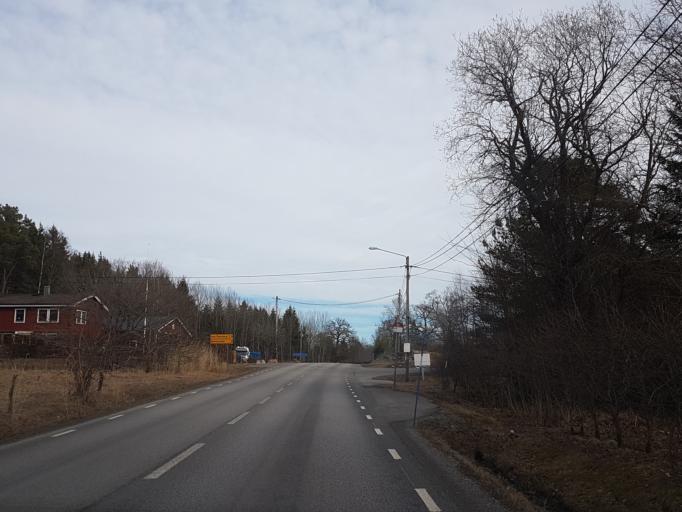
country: SE
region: Stockholm
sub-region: Norrtalje Kommun
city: Norrtalje
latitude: 59.6794
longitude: 18.7402
